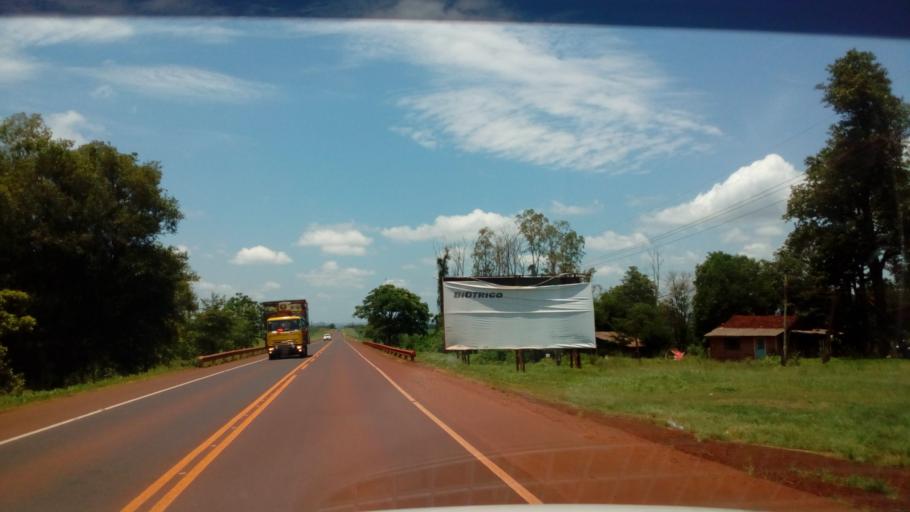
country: PY
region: Alto Parana
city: Naranjal
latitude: -25.9978
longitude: -55.1232
